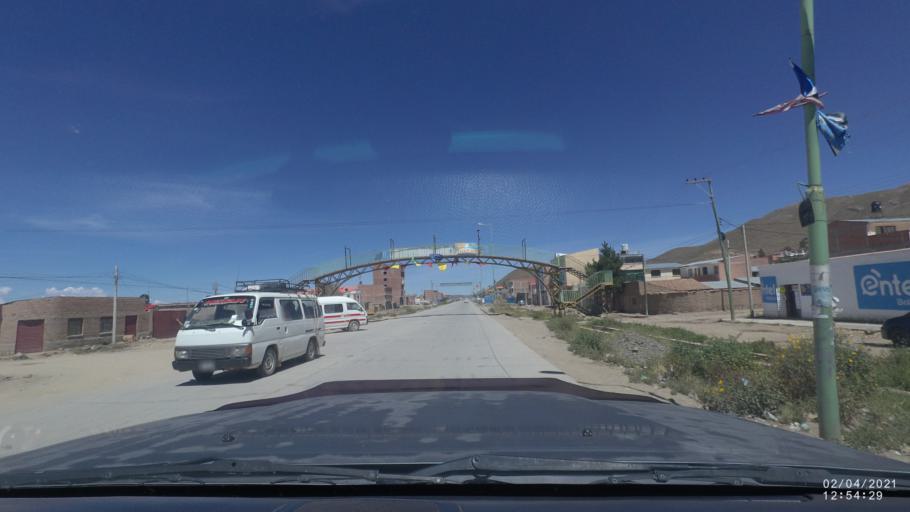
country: BO
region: Oruro
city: Oruro
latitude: -17.9986
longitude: -67.1357
